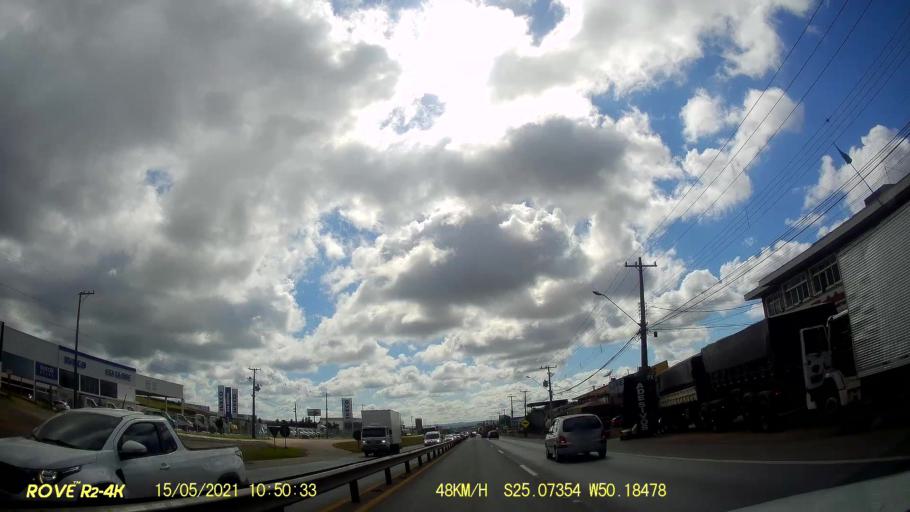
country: BR
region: Parana
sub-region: Ponta Grossa
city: Ponta Grossa
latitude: -25.0734
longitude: -50.1847
